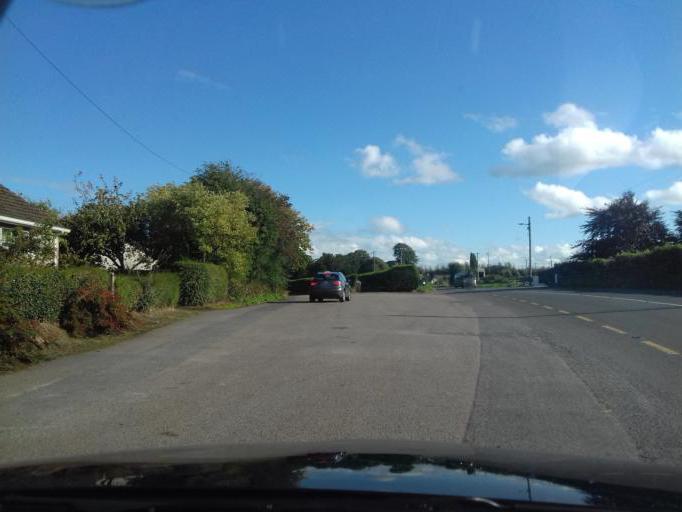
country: IE
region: Leinster
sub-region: Uibh Fhaili
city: Tullamore
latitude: 53.2567
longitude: -7.4824
